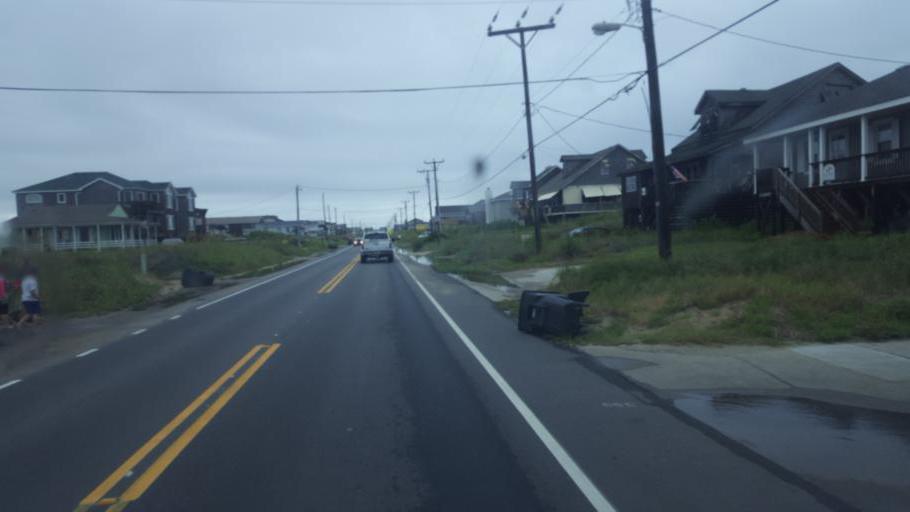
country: US
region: North Carolina
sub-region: Dare County
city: Kill Devil Hills
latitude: 36.0451
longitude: -75.6760
